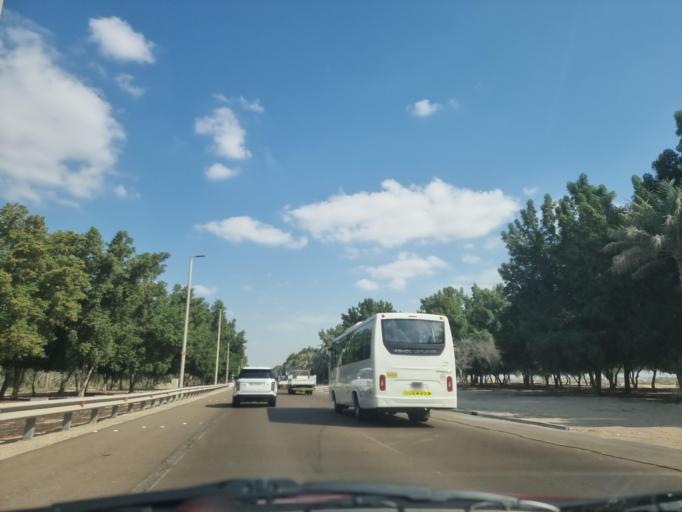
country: AE
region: Abu Dhabi
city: Abu Dhabi
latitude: 24.4089
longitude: 54.6319
